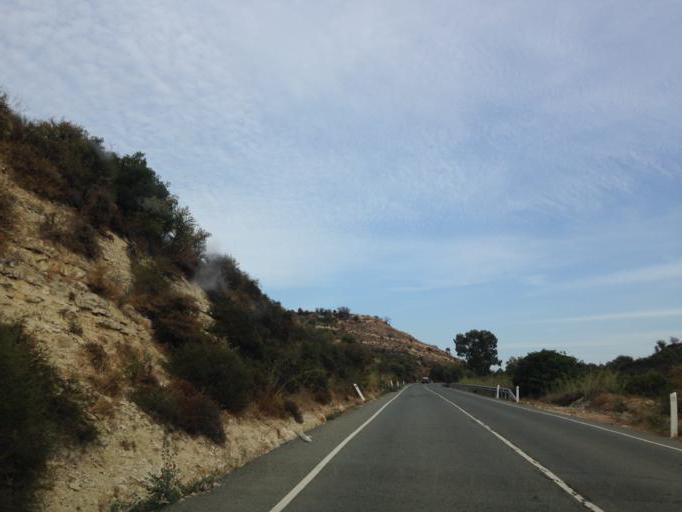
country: CY
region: Limassol
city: Pachna
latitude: 34.8015
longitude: 32.7942
